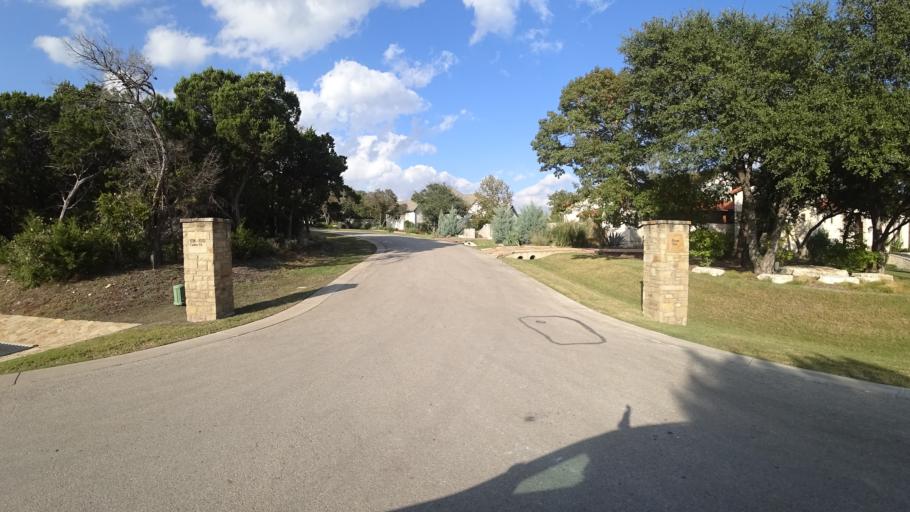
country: US
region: Texas
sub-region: Travis County
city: Barton Creek
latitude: 30.2776
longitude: -97.8740
